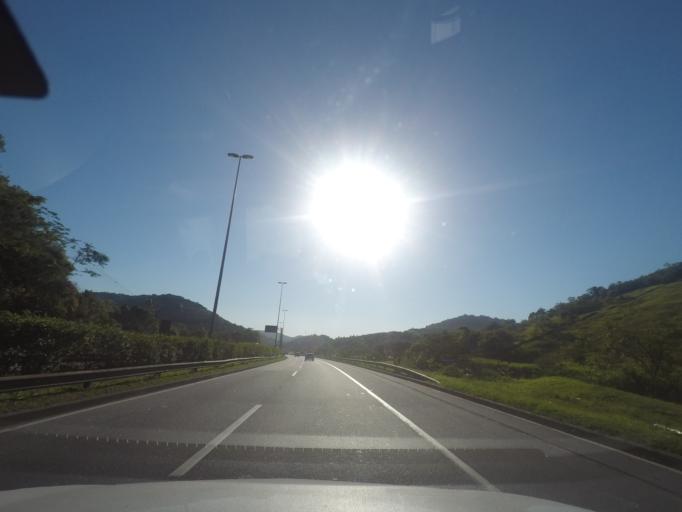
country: BR
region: Rio de Janeiro
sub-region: Petropolis
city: Petropolis
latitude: -22.6536
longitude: -43.1579
